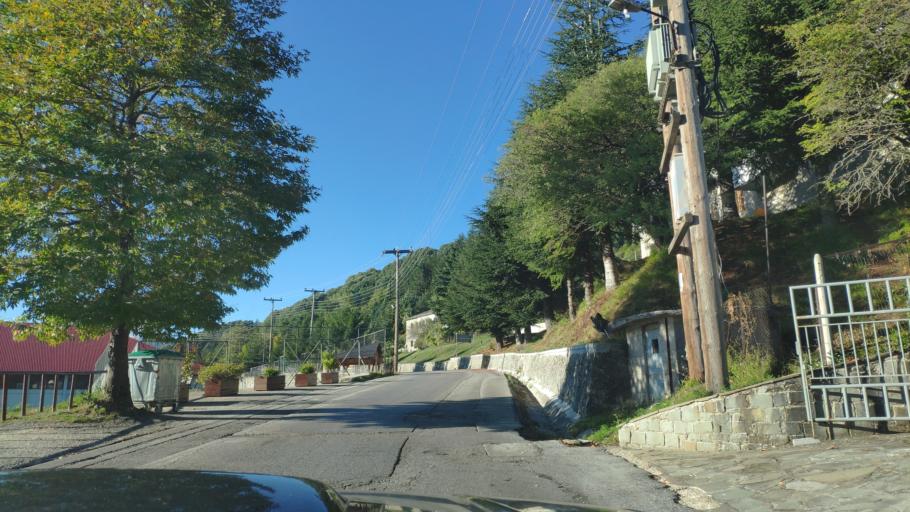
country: GR
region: Epirus
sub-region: Nomos Ioanninon
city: Metsovo
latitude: 39.7711
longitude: 21.1777
